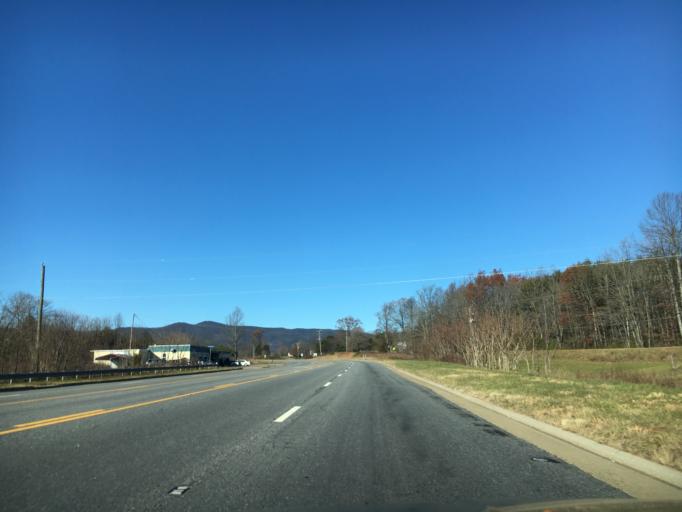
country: US
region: Virginia
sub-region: Patrick County
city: Patrick Springs
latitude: 36.6270
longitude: -80.1936
